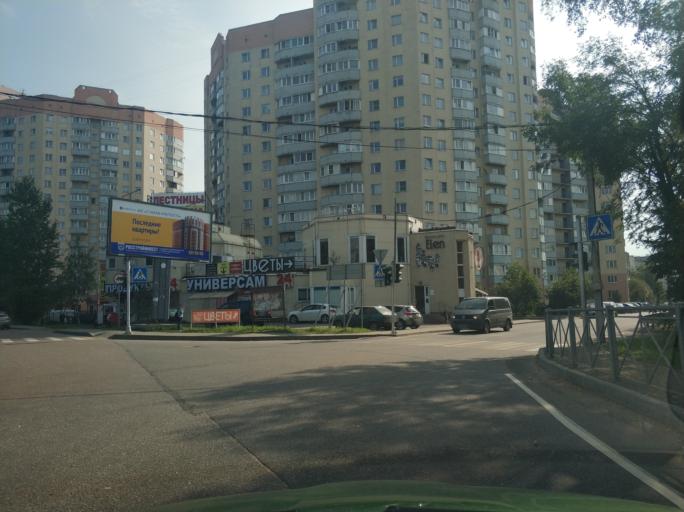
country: RU
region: Leningrad
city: Murino
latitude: 60.0471
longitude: 30.4606
